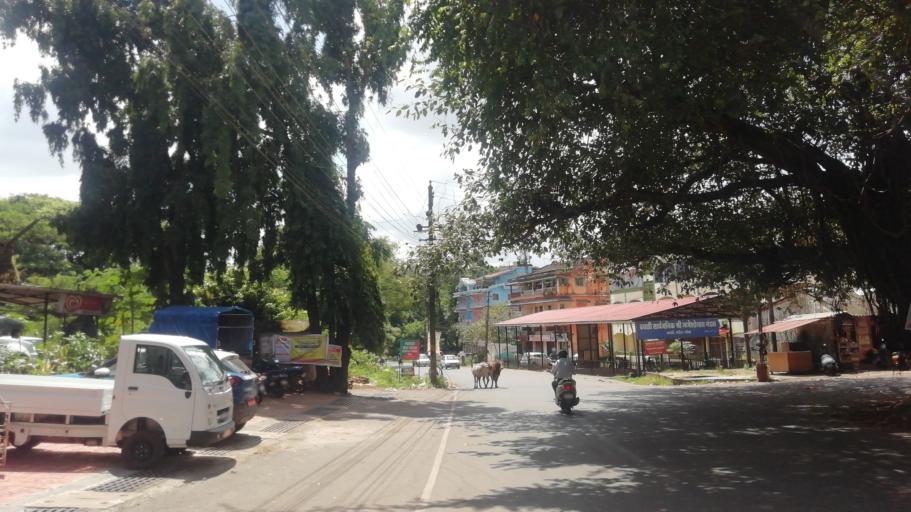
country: IN
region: Goa
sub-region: North Goa
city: Queula
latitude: 15.3866
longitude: 74.0036
